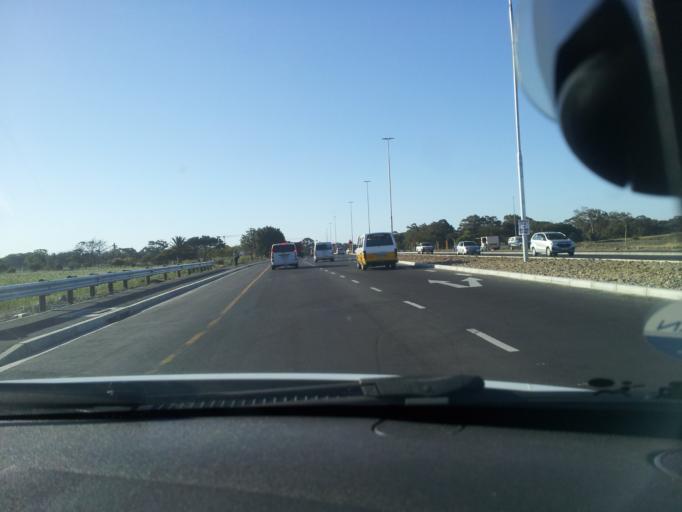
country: ZA
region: Western Cape
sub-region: Cape Winelands District Municipality
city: Stellenbosch
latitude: -34.0980
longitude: 18.8260
